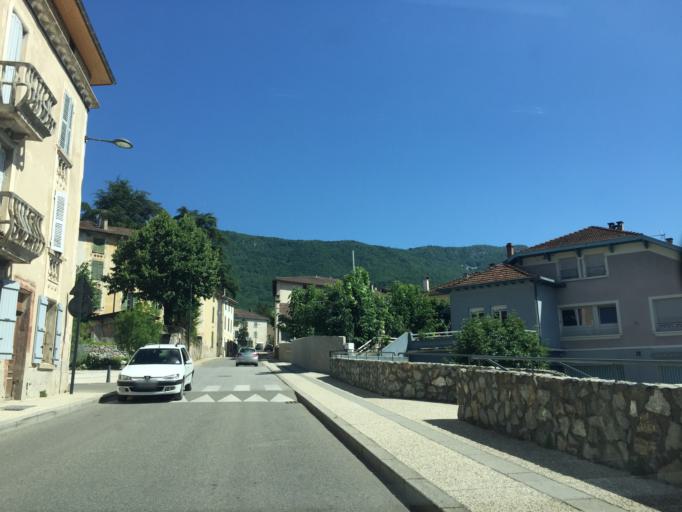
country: FR
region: Rhone-Alpes
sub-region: Departement de la Drome
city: Saint-Jean-en-Royans
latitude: 45.0205
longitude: 5.2916
